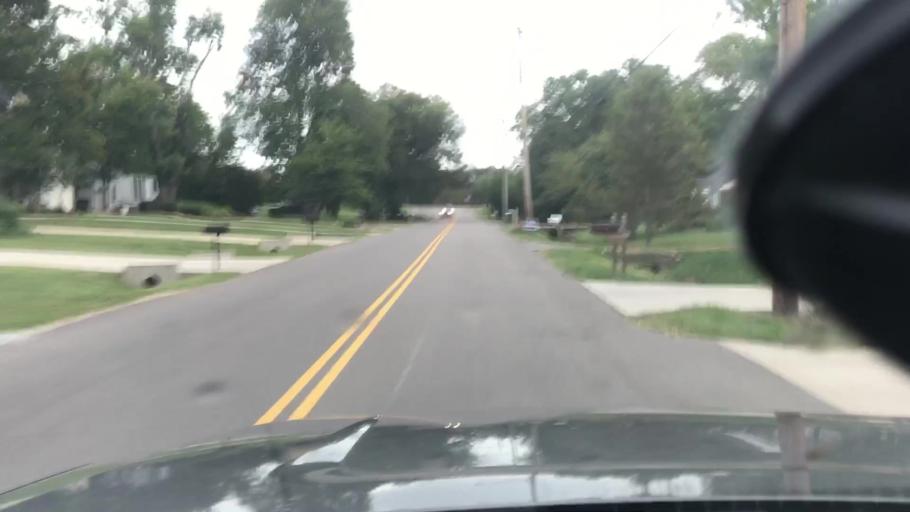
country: US
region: Tennessee
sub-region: Davidson County
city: Oak Hill
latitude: 36.1152
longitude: -86.7946
